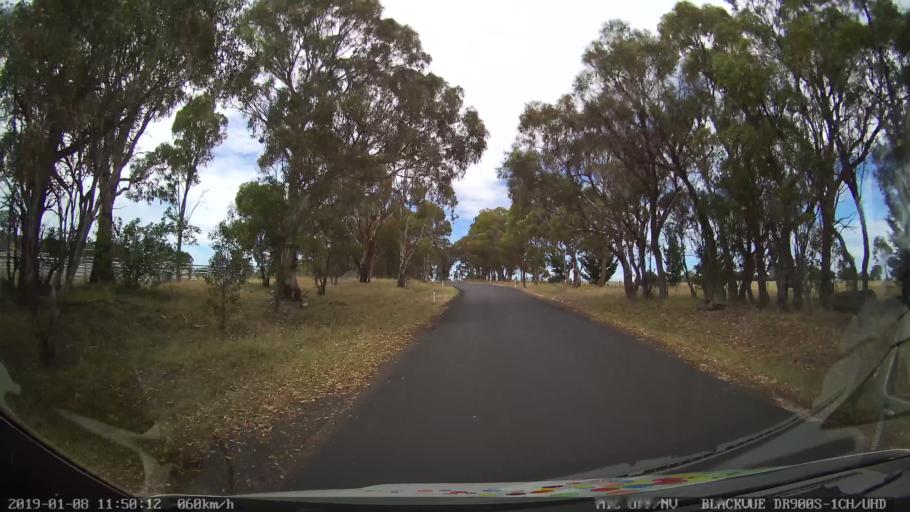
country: AU
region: New South Wales
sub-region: Armidale Dumaresq
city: Armidale
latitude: -30.3806
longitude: 151.5579
